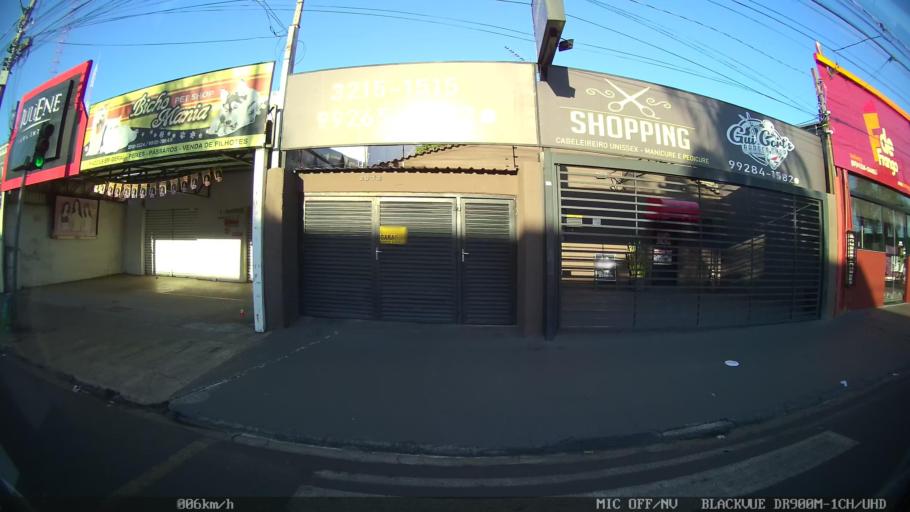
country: BR
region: Sao Paulo
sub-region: Sao Jose Do Rio Preto
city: Sao Jose do Rio Preto
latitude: -20.7799
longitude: -49.3675
